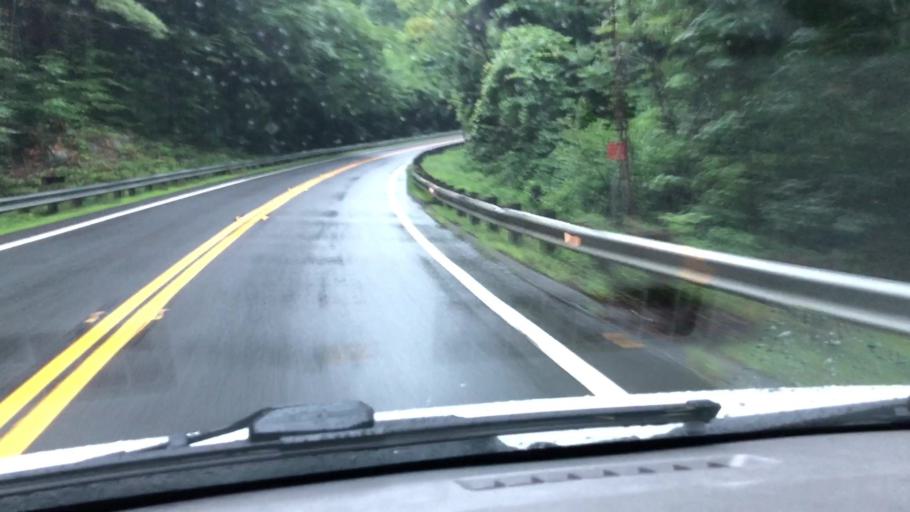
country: US
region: Massachusetts
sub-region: Hampshire County
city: Westhampton
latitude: 42.2837
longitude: -72.8698
